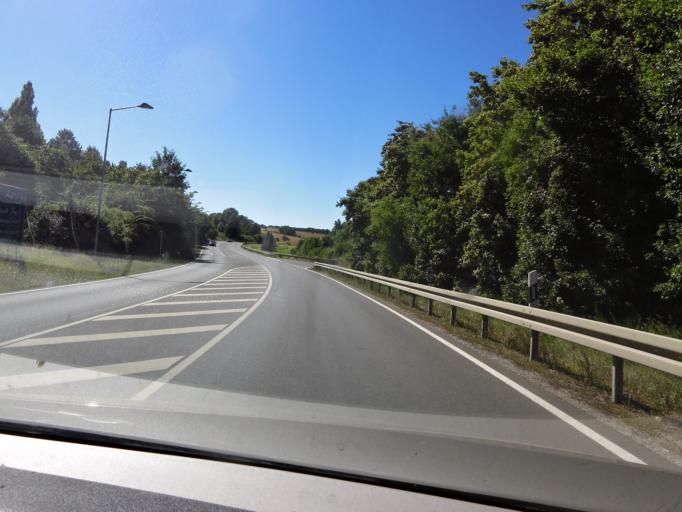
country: DE
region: Bavaria
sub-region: Regierungsbezirk Unterfranken
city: Kitzingen
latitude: 49.7410
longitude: 10.1413
